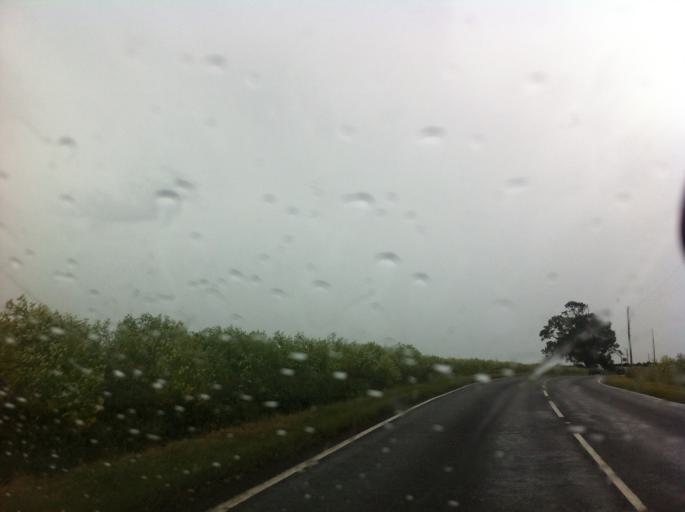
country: GB
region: England
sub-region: Northamptonshire
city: Irchester
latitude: 52.2722
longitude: -0.6761
